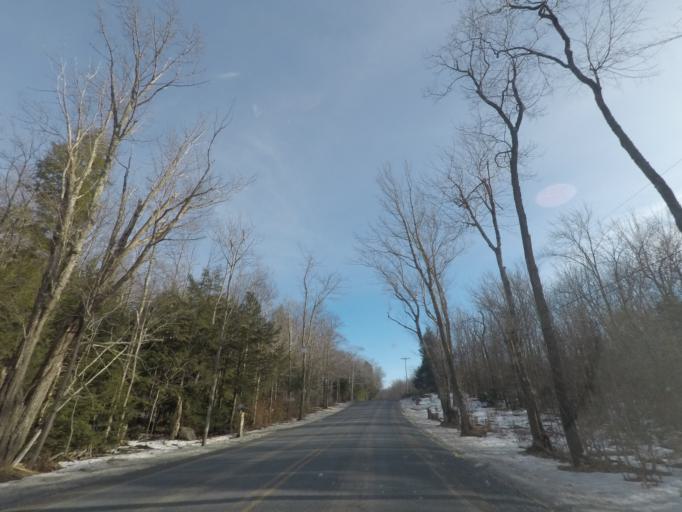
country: US
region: New York
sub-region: Rensselaer County
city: Poestenkill
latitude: 42.7513
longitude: -73.4171
